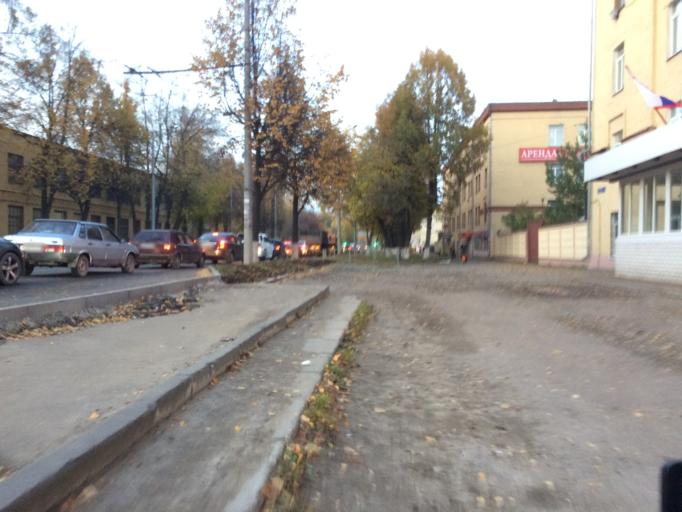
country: RU
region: Mariy-El
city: Yoshkar-Ola
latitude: 56.6145
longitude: 47.8827
